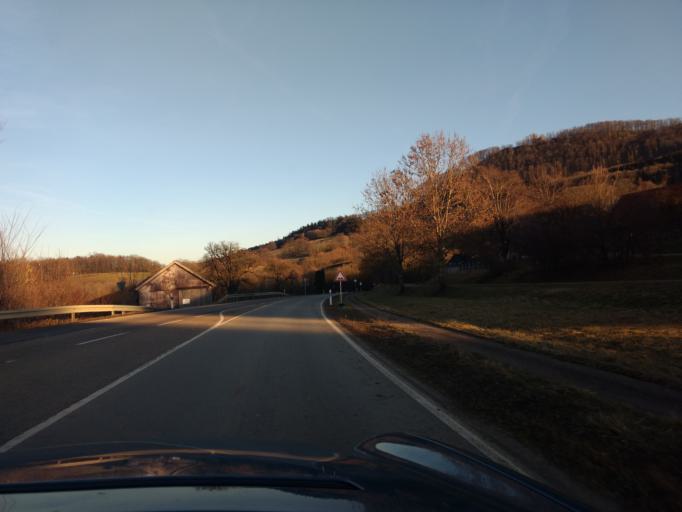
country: DE
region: Baden-Wuerttemberg
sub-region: Regierungsbezirk Stuttgart
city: Schwabisch Gmund
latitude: 48.7654
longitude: 9.7778
